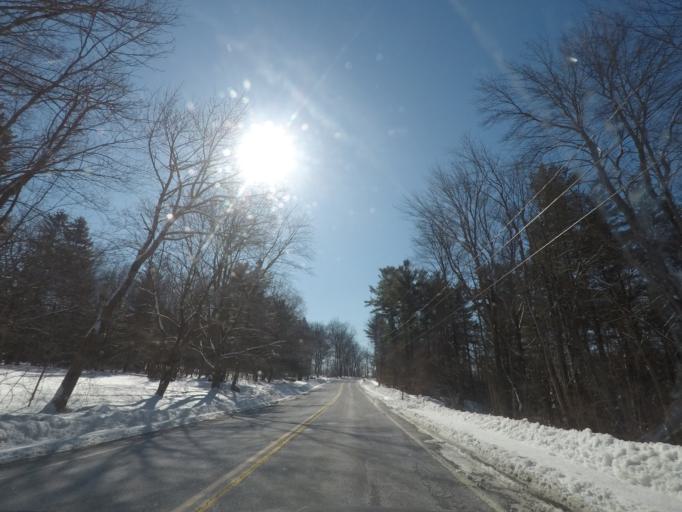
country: US
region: New York
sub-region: Saratoga County
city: Ballston Spa
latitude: 42.9964
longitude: -73.8268
